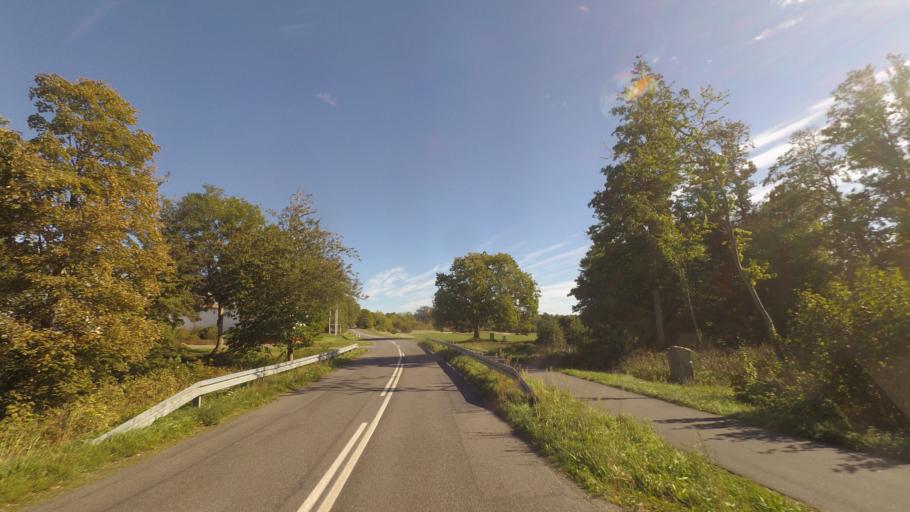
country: DK
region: Capital Region
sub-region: Bornholm Kommune
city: Nexo
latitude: 55.0028
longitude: 15.0289
